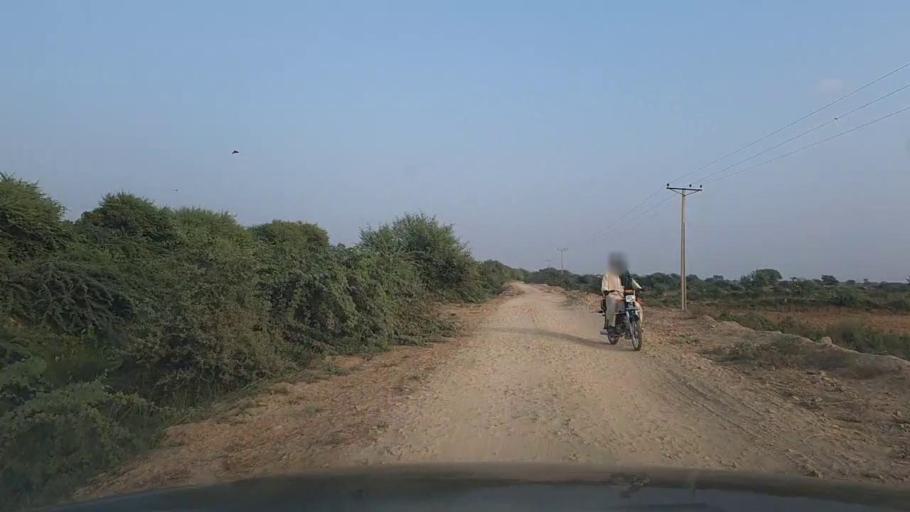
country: PK
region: Sindh
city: Mirpur Batoro
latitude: 24.5450
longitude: 68.3564
